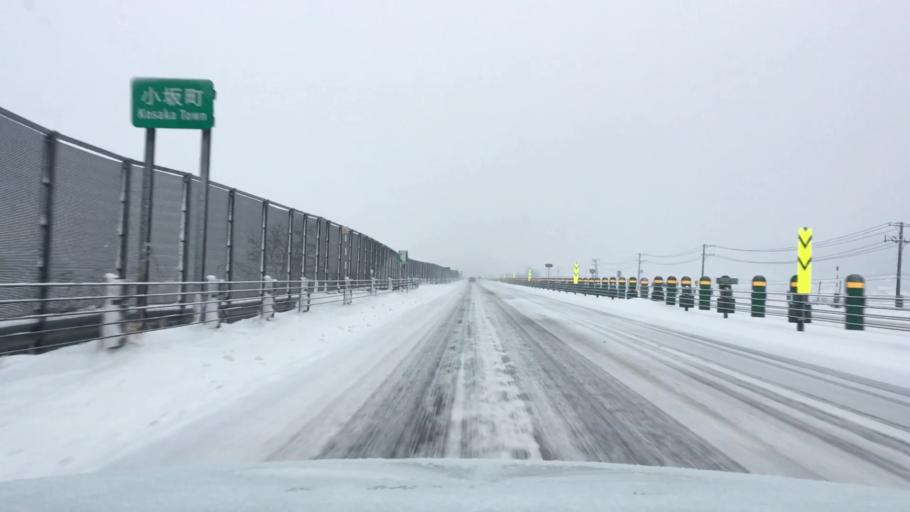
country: JP
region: Akita
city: Hanawa
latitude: 40.2839
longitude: 140.7600
